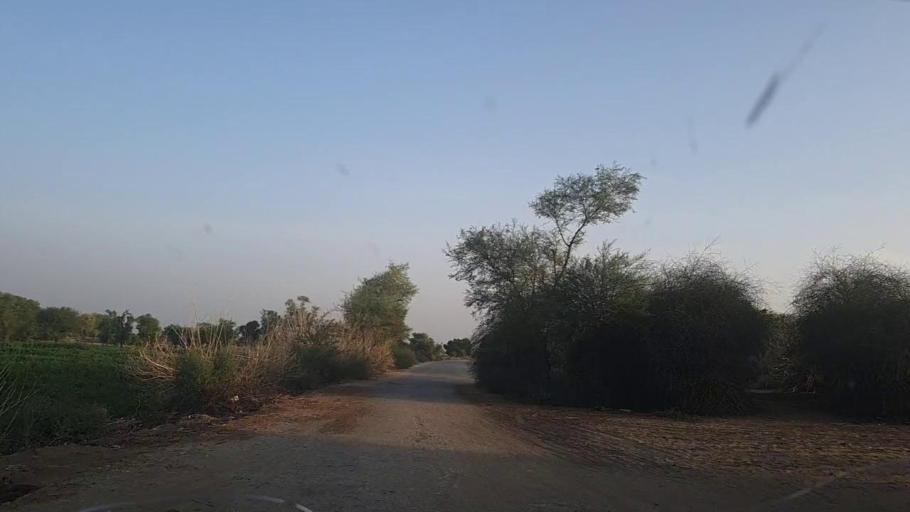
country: PK
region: Sindh
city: Khanpur
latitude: 27.6236
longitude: 69.4448
